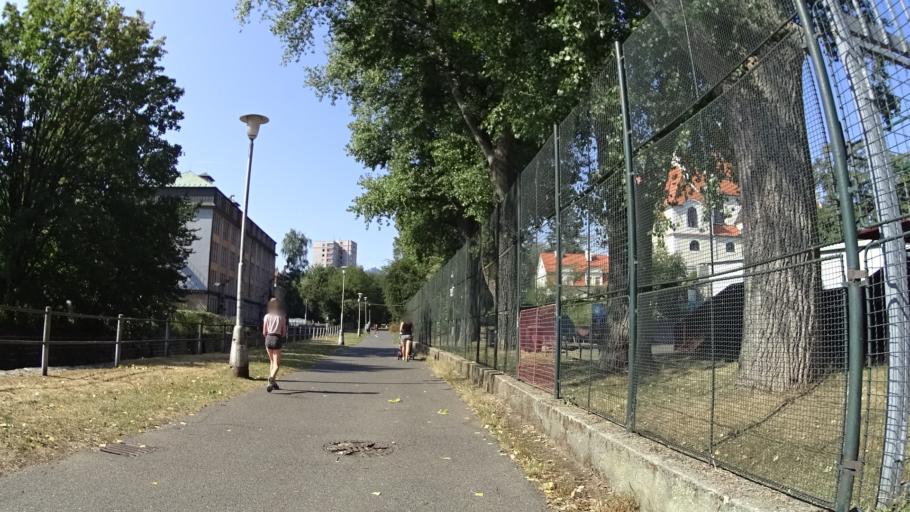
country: CZ
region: Liberecky
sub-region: Okres Liberec
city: Liberec
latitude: 50.7678
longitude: 15.0494
